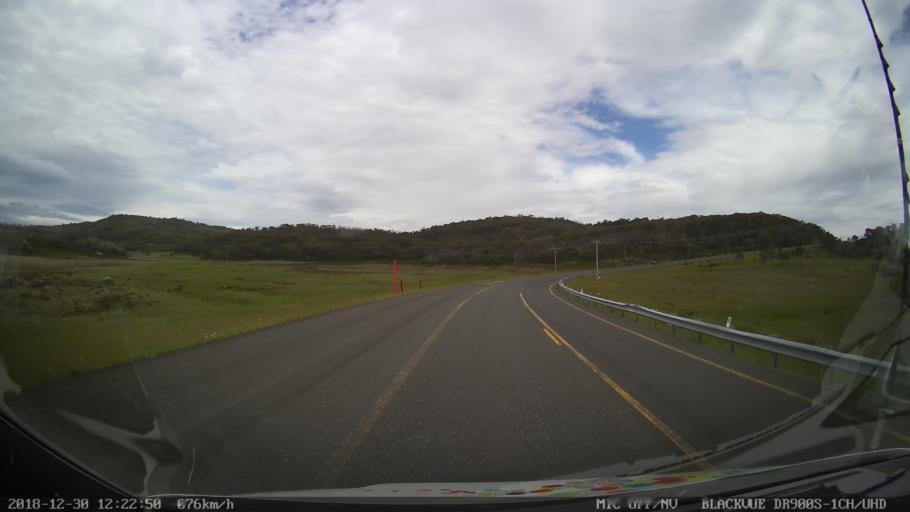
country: AU
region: New South Wales
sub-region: Snowy River
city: Jindabyne
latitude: -36.3613
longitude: 148.5069
